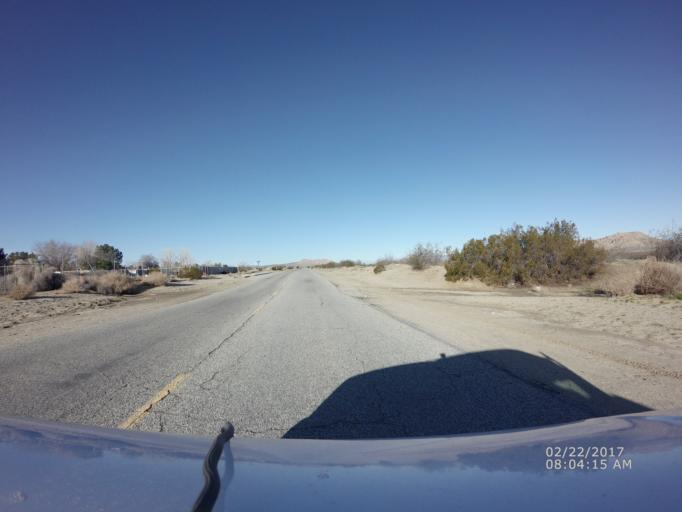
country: US
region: California
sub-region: Los Angeles County
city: Lake Los Angeles
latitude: 34.6313
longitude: -117.8305
